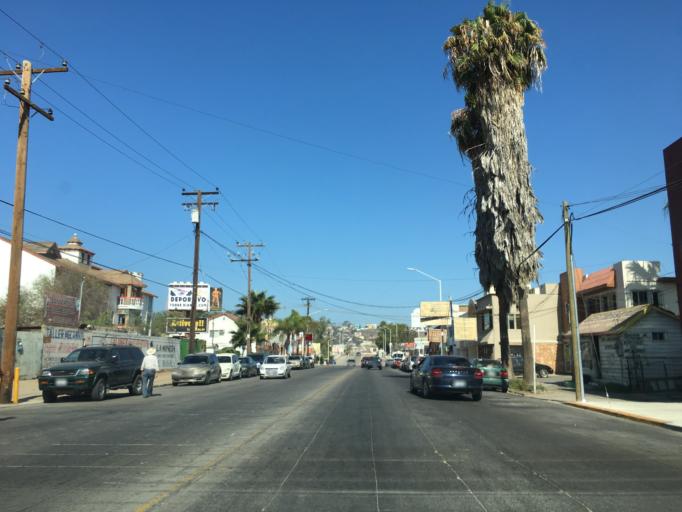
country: MX
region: Baja California
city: Ensenada
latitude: 31.8626
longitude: -116.6154
